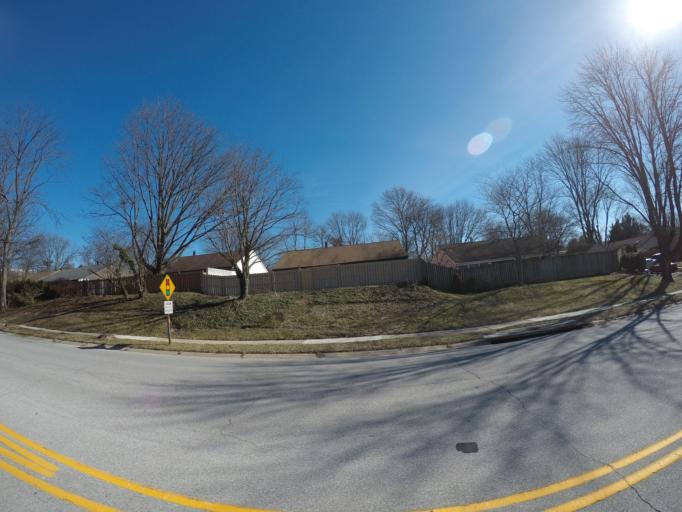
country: US
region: Maryland
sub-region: Howard County
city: Columbia
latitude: 39.2254
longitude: -76.8175
